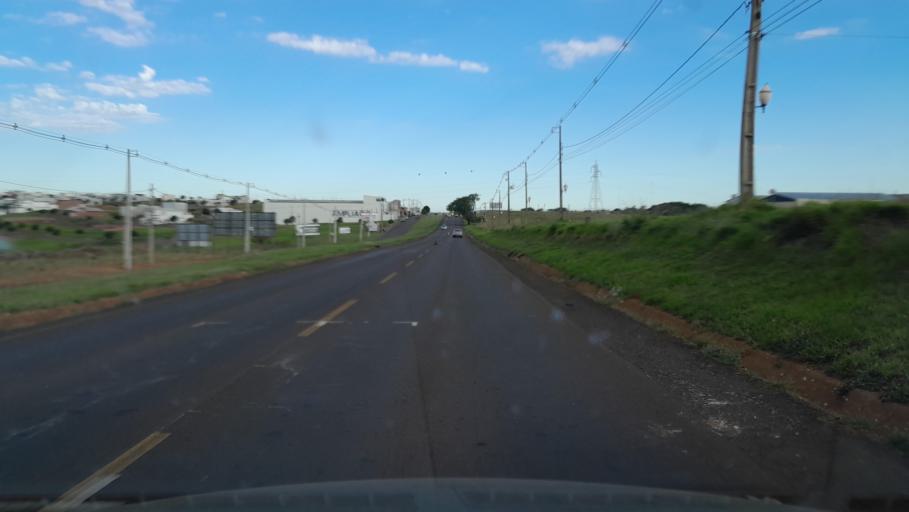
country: BR
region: Parana
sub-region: Umuarama
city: Umuarama
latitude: -23.7568
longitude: -53.2717
